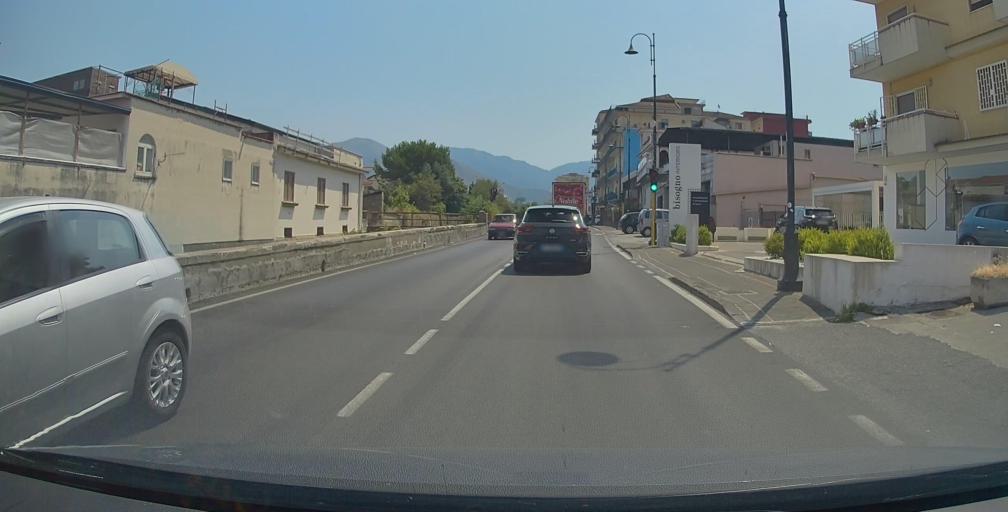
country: IT
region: Campania
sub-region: Provincia di Salerno
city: Nocera Inferiore
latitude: 40.7409
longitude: 14.6527
